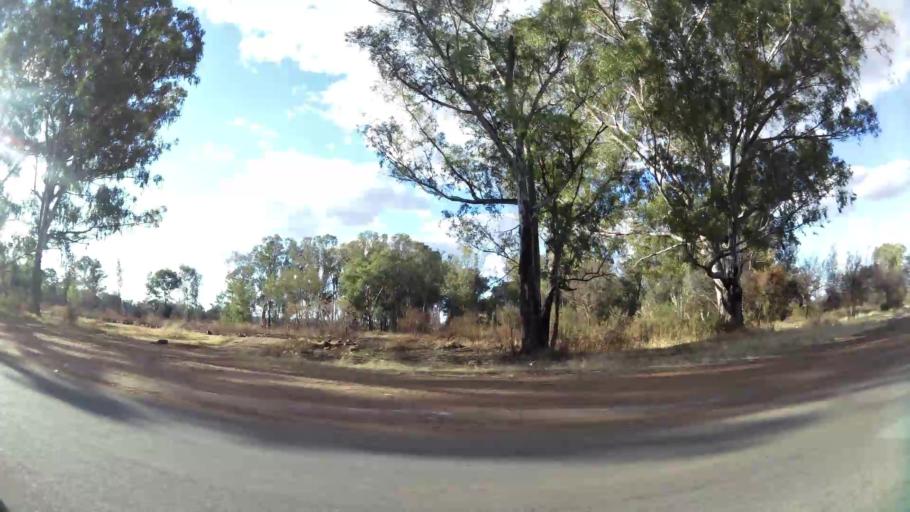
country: ZA
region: North-West
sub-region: Dr Kenneth Kaunda District Municipality
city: Potchefstroom
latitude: -26.7098
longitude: 27.0802
